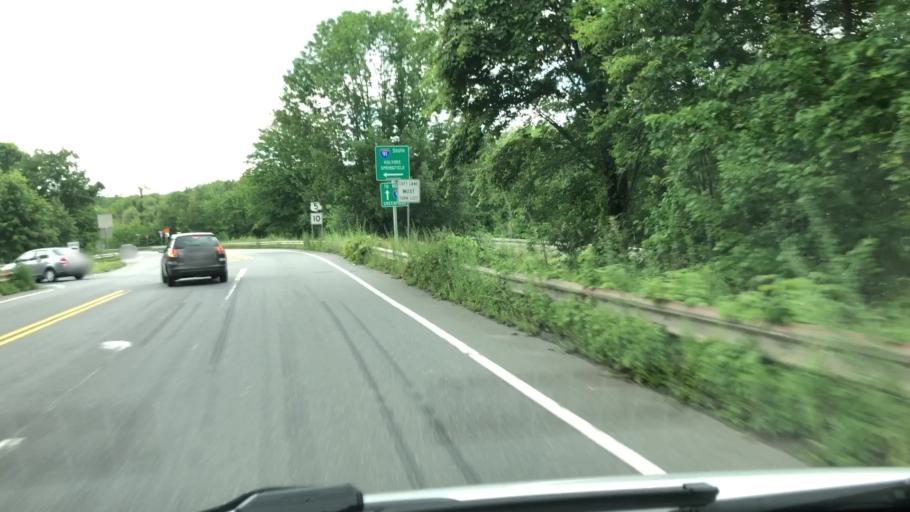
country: US
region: Massachusetts
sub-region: Franklin County
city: South Deerfield
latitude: 42.4664
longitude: -72.6171
